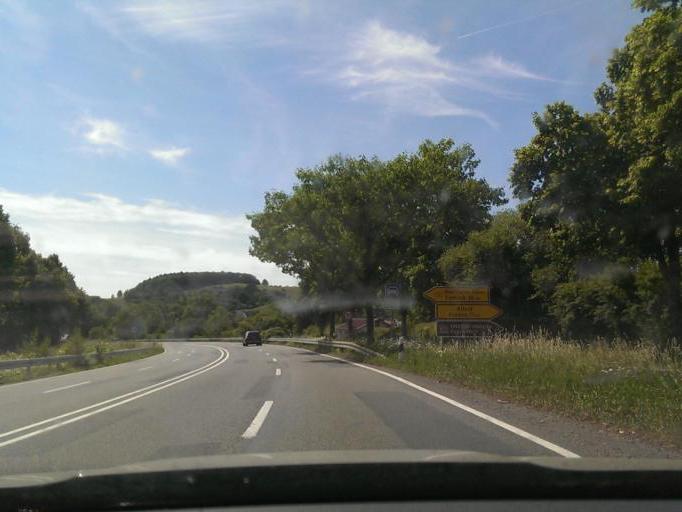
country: DE
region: Lower Saxony
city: Alfeld
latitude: 51.9904
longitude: 9.7999
